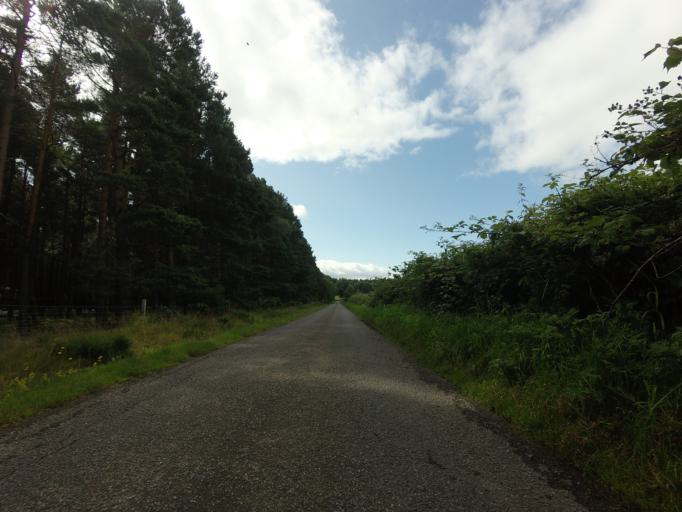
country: GB
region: Scotland
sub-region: Highland
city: Nairn
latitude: 57.5631
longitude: -3.8671
